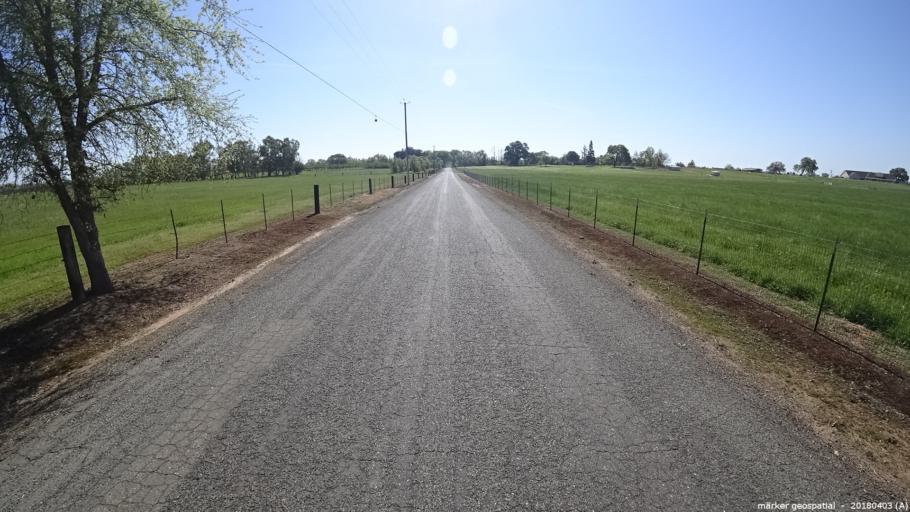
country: US
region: California
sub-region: Sacramento County
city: Wilton
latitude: 38.4357
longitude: -121.2248
